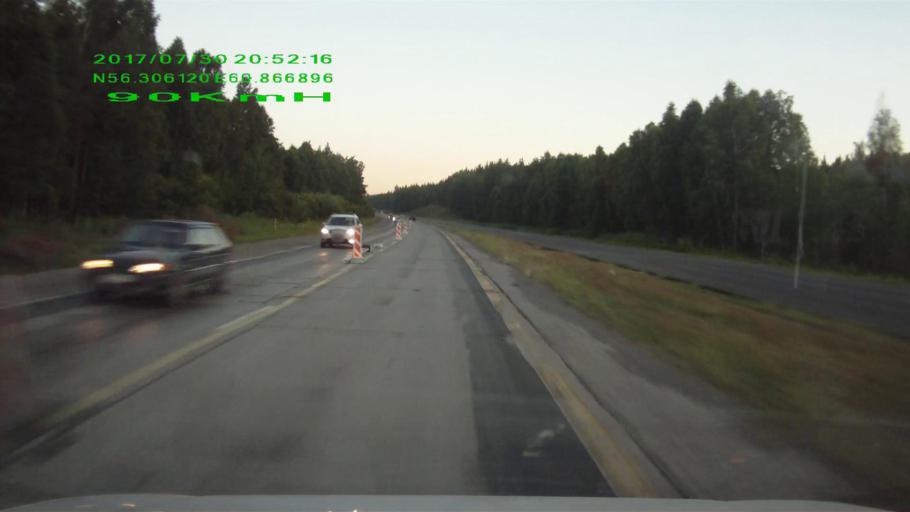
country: RU
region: Sverdlovsk
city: Shchelkun
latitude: 56.3057
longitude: 60.8668
